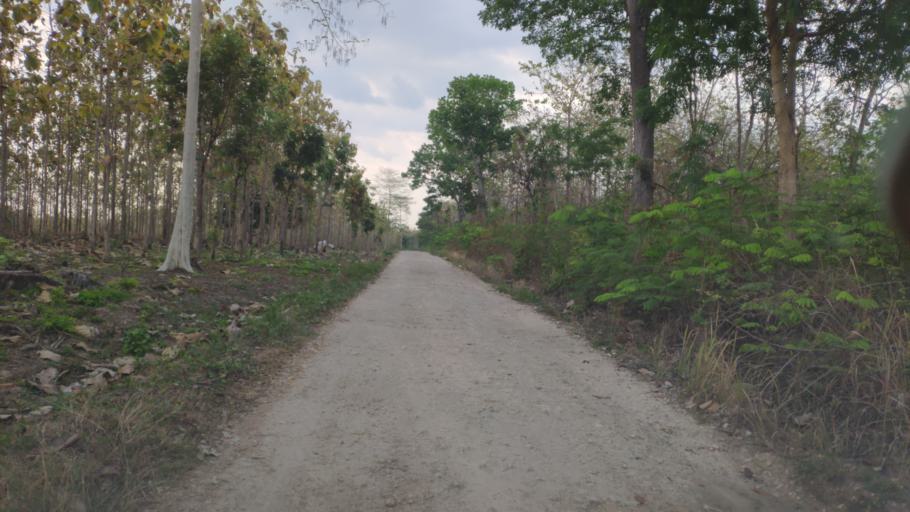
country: ID
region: Central Java
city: Randublatung
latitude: -7.2832
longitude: 111.2925
